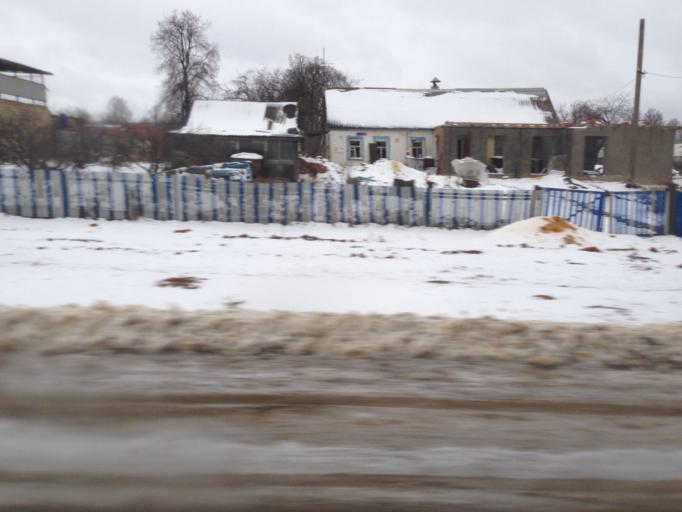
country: RU
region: Tula
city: Bolokhovo
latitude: 54.0487
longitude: 37.8268
